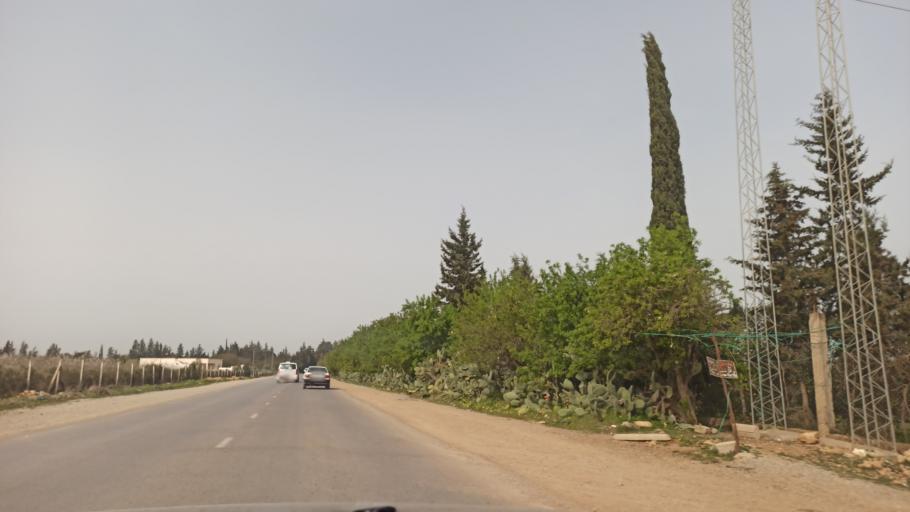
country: TN
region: Zaghwan
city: Zaghouan
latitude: 36.4209
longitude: 10.0992
